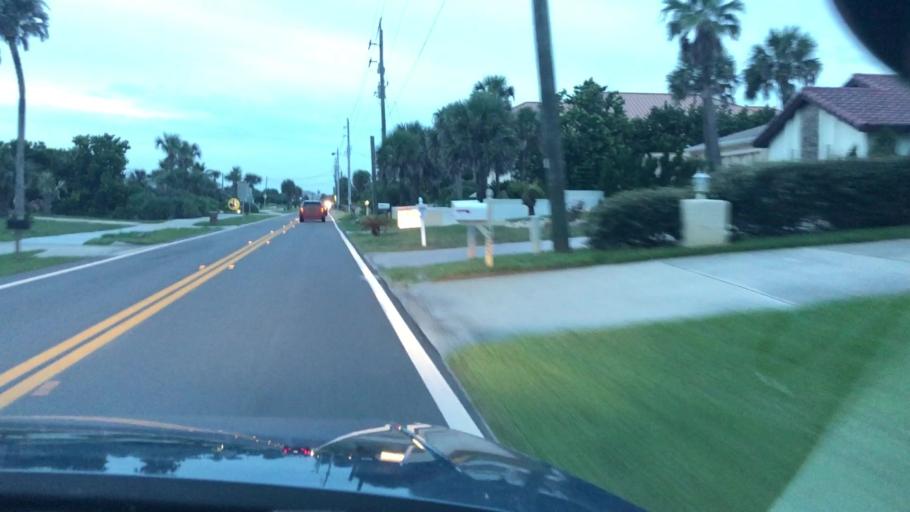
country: US
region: Florida
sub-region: Volusia County
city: Ponce Inlet
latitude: 29.1205
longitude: -80.9514
